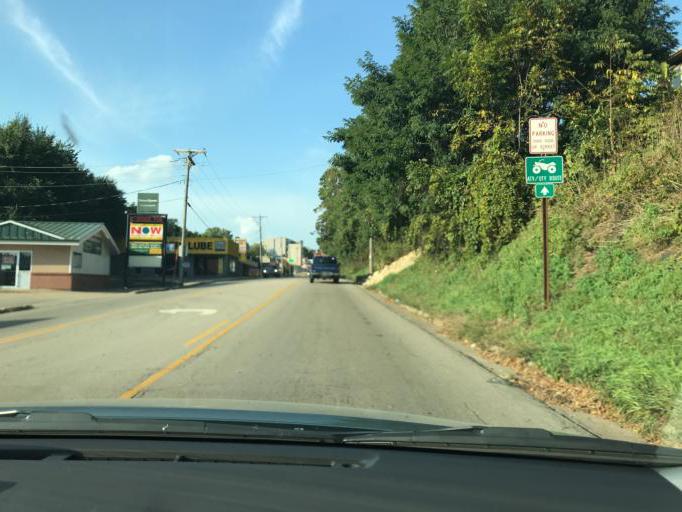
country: US
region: Wisconsin
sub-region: Grant County
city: Platteville
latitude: 42.7298
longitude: -90.4760
